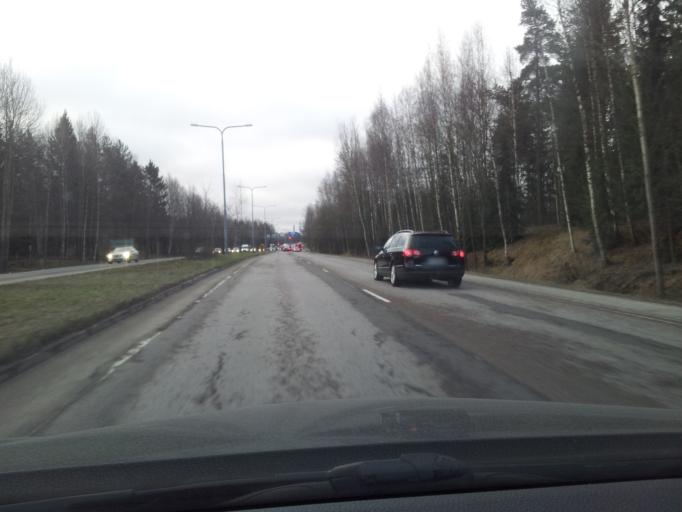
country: FI
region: Uusimaa
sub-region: Helsinki
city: Teekkarikylae
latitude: 60.2296
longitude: 24.8692
